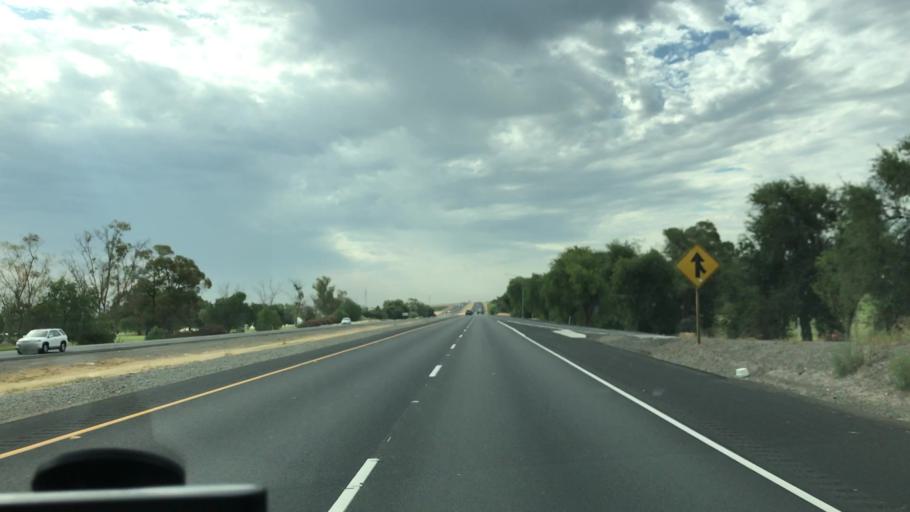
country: US
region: California
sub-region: San Joaquin County
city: Tracy
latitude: 37.6347
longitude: -121.3956
